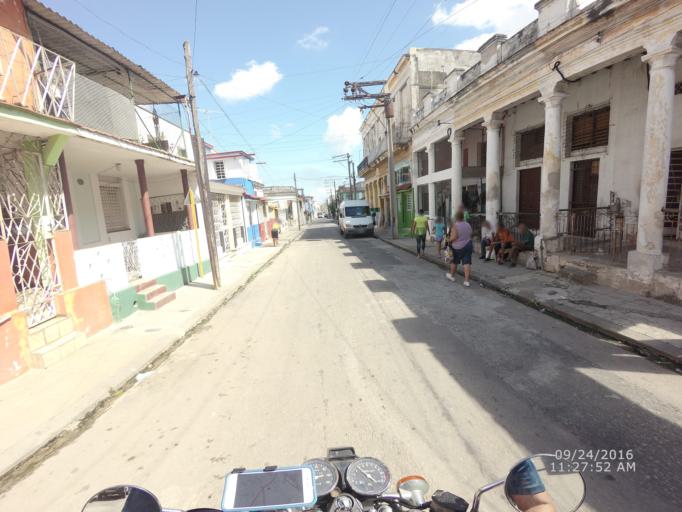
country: CU
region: La Habana
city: Cerro
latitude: 23.1099
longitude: -82.3648
